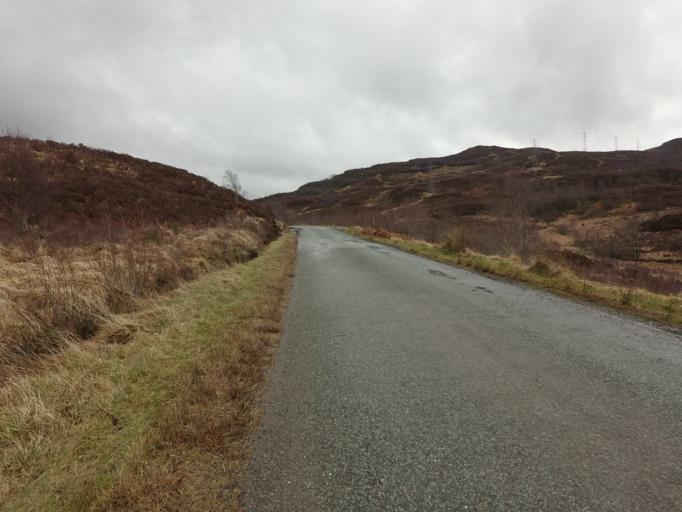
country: GB
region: Scotland
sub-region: West Dunbartonshire
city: Balloch
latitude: 56.2459
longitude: -4.5838
